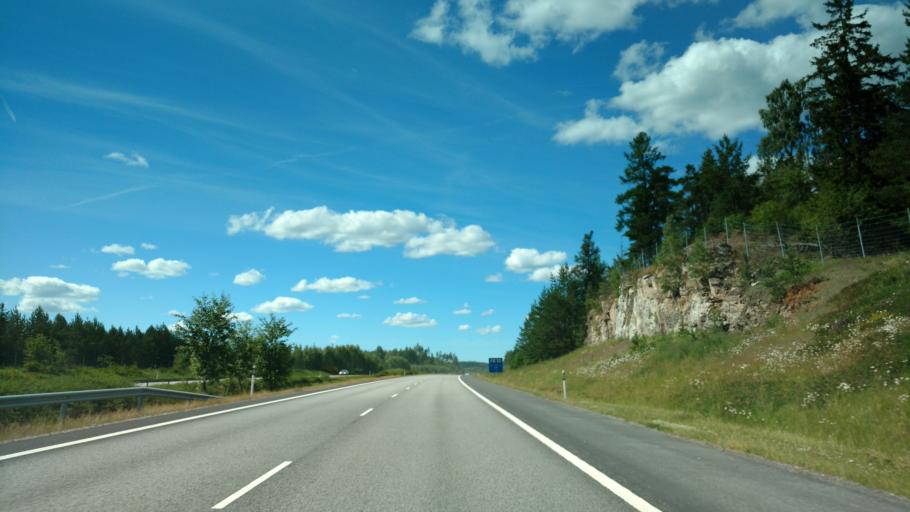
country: FI
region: Varsinais-Suomi
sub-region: Turku
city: Paimio
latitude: 60.4369
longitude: 22.6356
